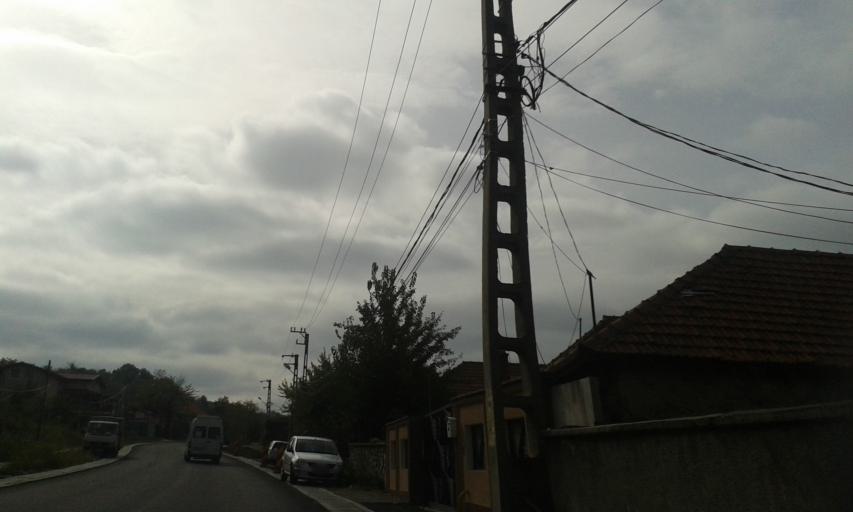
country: RO
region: Gorj
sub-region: Comuna Bumbesti-Jiu
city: Bumbesti-Jiu
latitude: 45.1873
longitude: 23.3874
